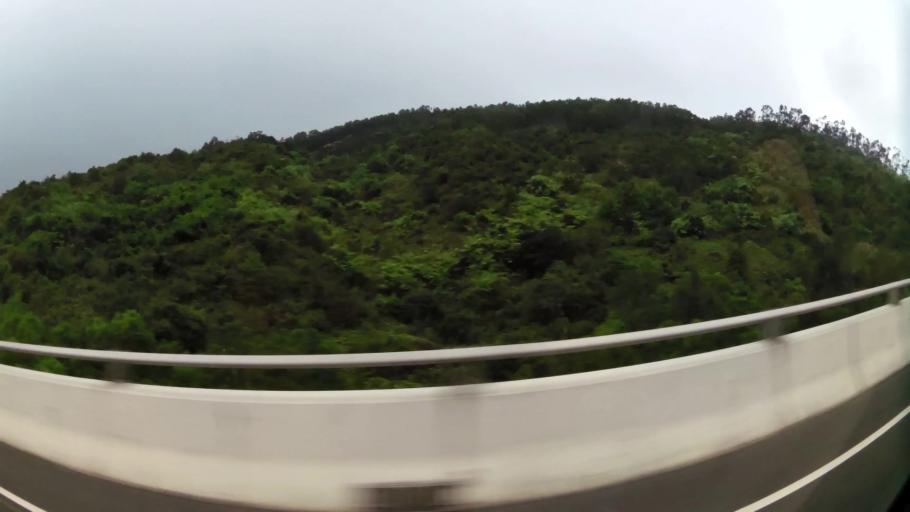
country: HK
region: Tsuen Wan
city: Tsuen Wan
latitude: 22.3600
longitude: 114.0852
